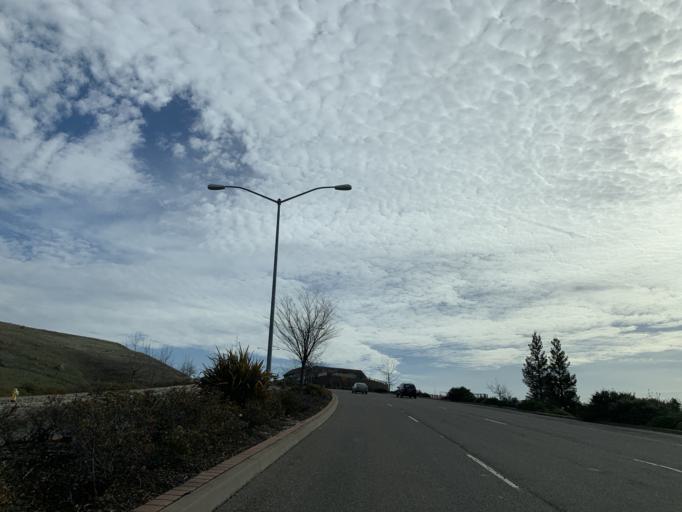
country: US
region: California
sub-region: El Dorado County
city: El Dorado Hills
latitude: 38.6473
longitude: -121.1019
